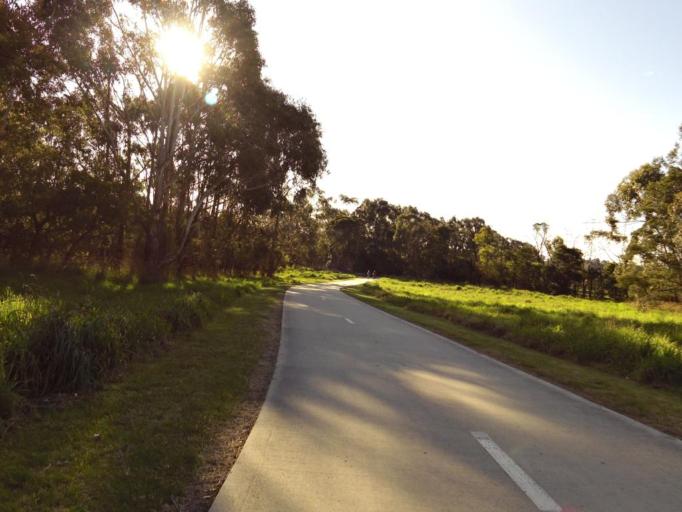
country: AU
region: Victoria
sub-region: Knox
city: Wantirna
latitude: -37.8540
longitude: 145.2122
